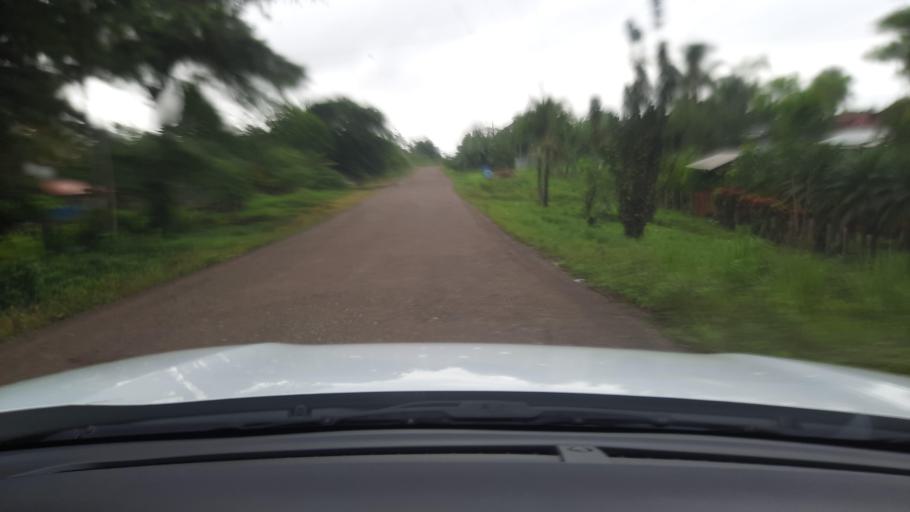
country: CR
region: Alajuela
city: San Jose
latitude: 11.0029
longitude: -85.3008
